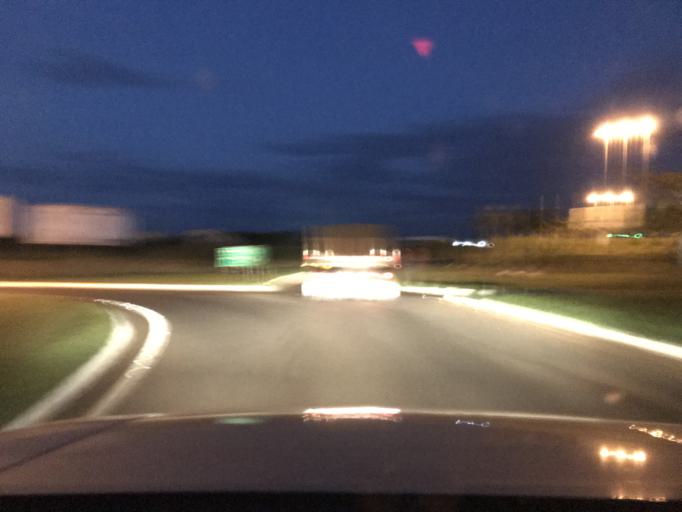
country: PY
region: Canindeyu
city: Salto del Guaira
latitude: -24.1064
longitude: -54.2395
